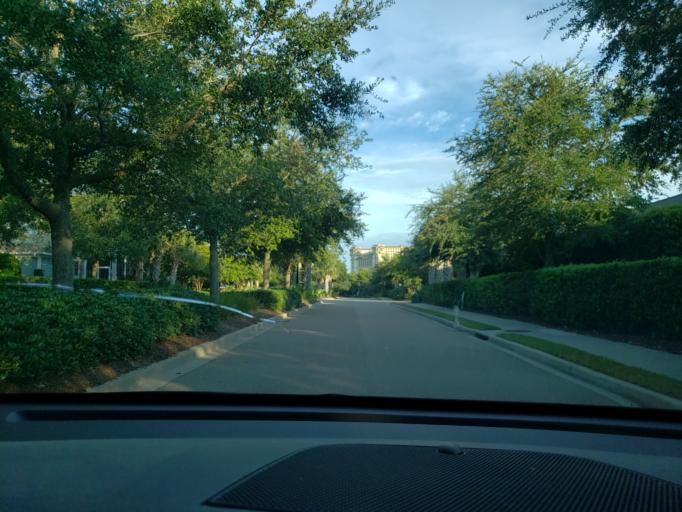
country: US
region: South Carolina
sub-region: Horry County
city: North Myrtle Beach
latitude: 33.7948
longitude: -78.7408
